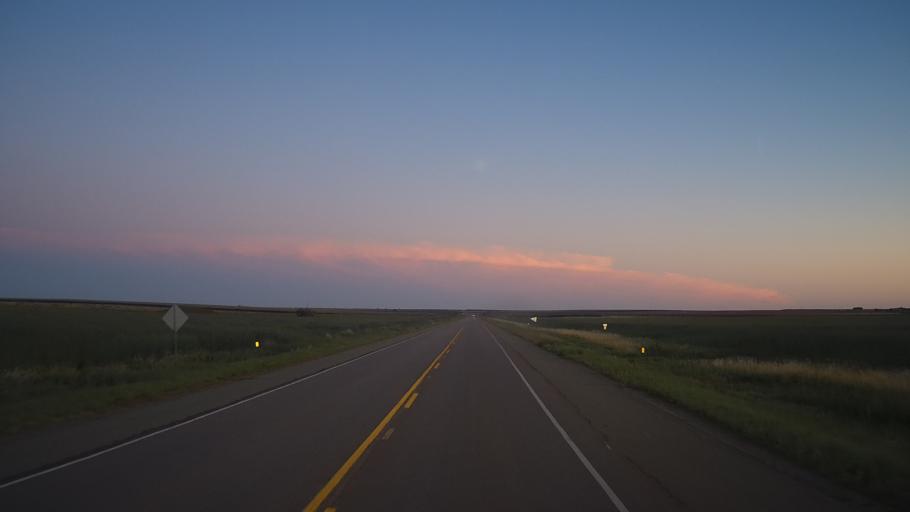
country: US
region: South Dakota
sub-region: Buffalo County
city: Fort Thompson
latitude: 43.8739
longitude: -99.6058
